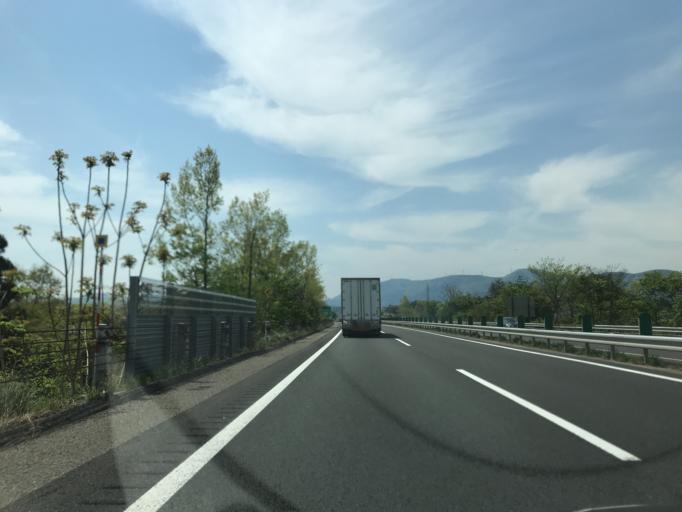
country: JP
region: Miyagi
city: Shiroishi
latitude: 38.0304
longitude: 140.6259
